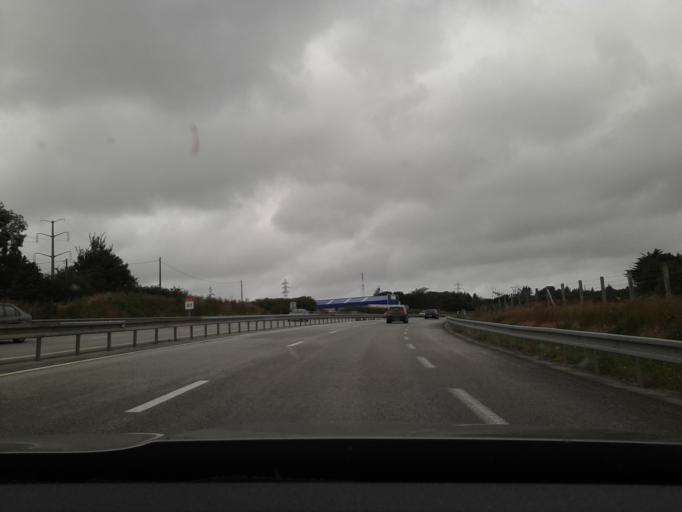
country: FR
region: Lower Normandy
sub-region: Departement de la Manche
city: La Glacerie
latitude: 49.5867
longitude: -1.5961
